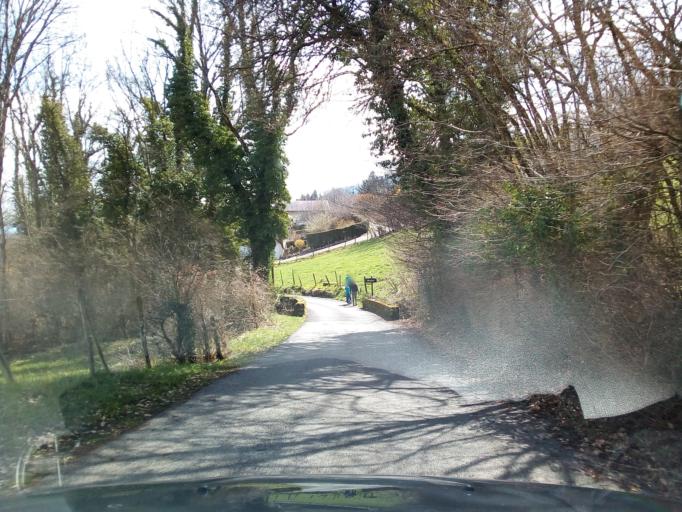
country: FR
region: Rhone-Alpes
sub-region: Departement de la Savoie
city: Saint-Baldoph
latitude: 45.5255
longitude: 5.9490
